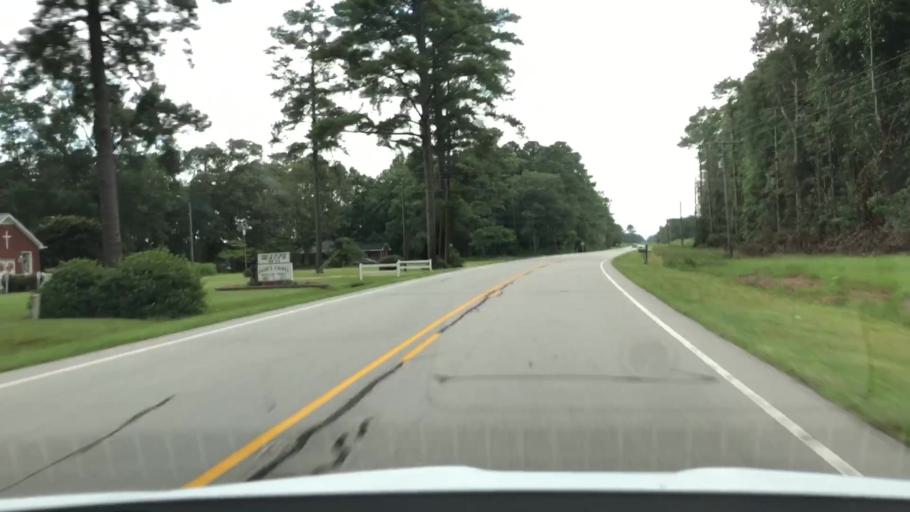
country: US
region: North Carolina
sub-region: Lenoir County
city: Kinston
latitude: 35.1210
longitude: -77.5171
